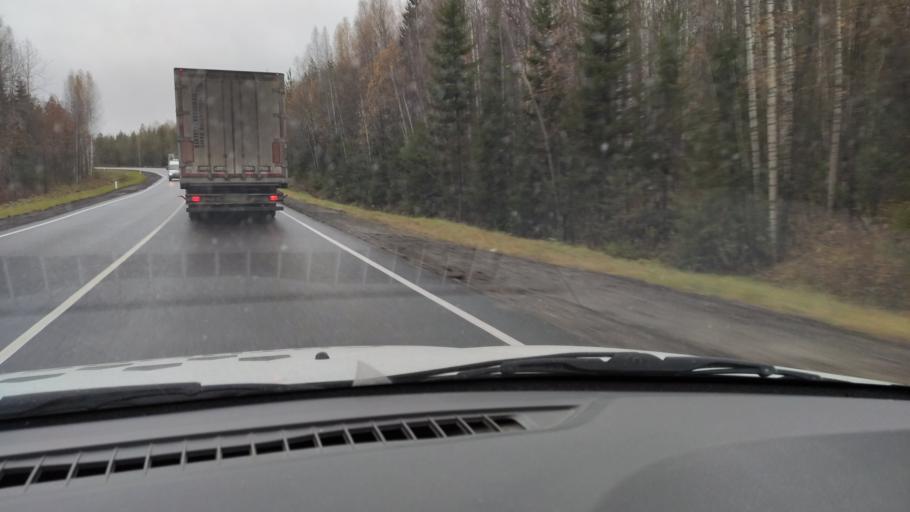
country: RU
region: Kirov
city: Omutninsk
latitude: 58.7475
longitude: 52.0612
